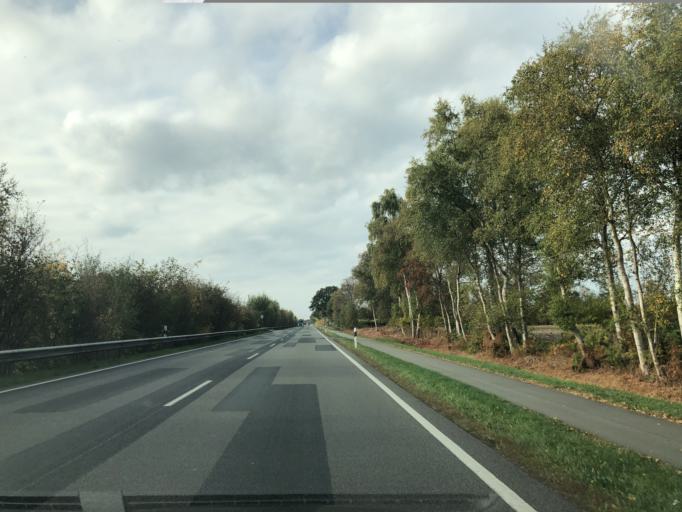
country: DE
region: Lower Saxony
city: Friesoythe
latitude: 53.0909
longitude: 7.8671
